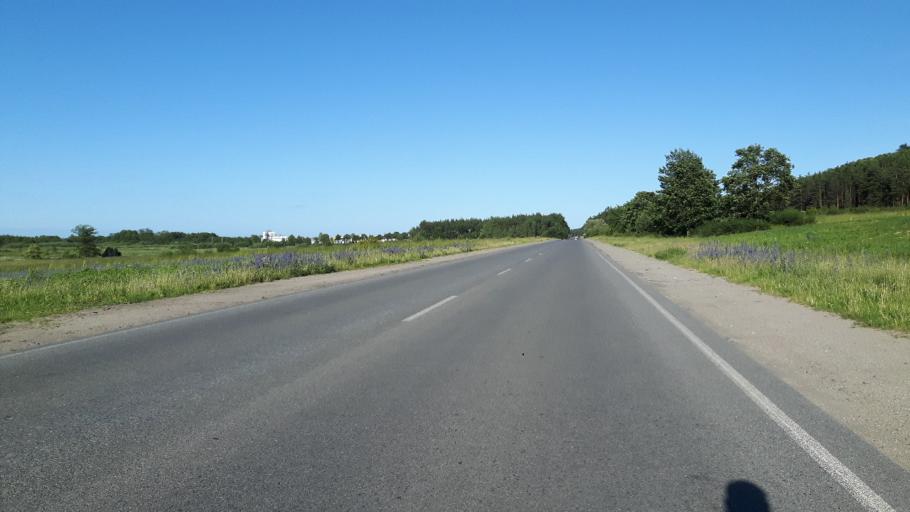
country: PL
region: Pomeranian Voivodeship
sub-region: Powiat pucki
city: Kosakowo
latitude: 54.6049
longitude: 18.4420
